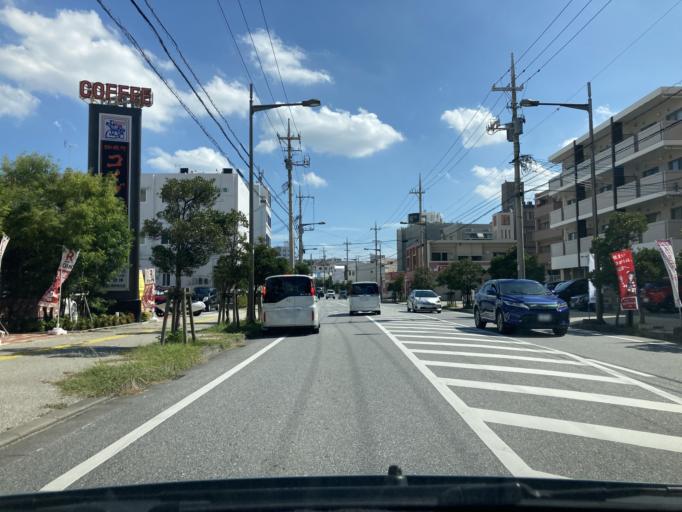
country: JP
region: Okinawa
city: Ginowan
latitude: 26.2706
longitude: 127.7315
